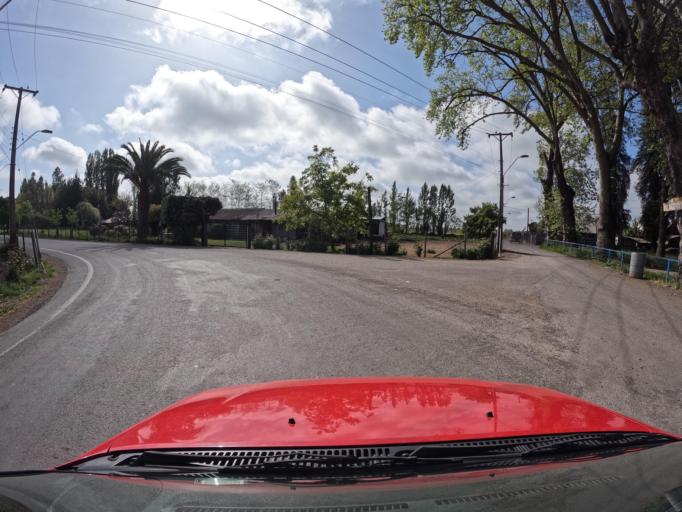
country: CL
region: Maule
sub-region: Provincia de Curico
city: Teno
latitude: -34.8833
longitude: -71.2271
